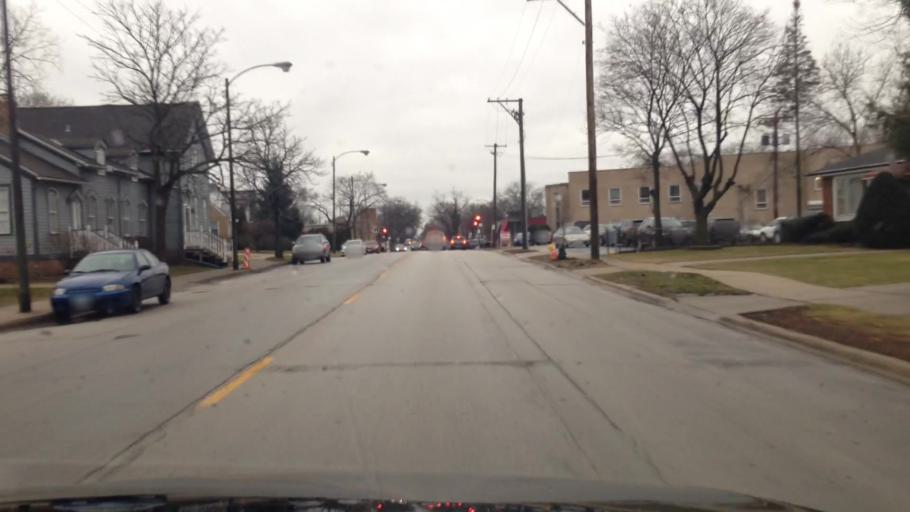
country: US
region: Illinois
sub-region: Cook County
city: Park Ridge
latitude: 41.9947
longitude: -87.8219
